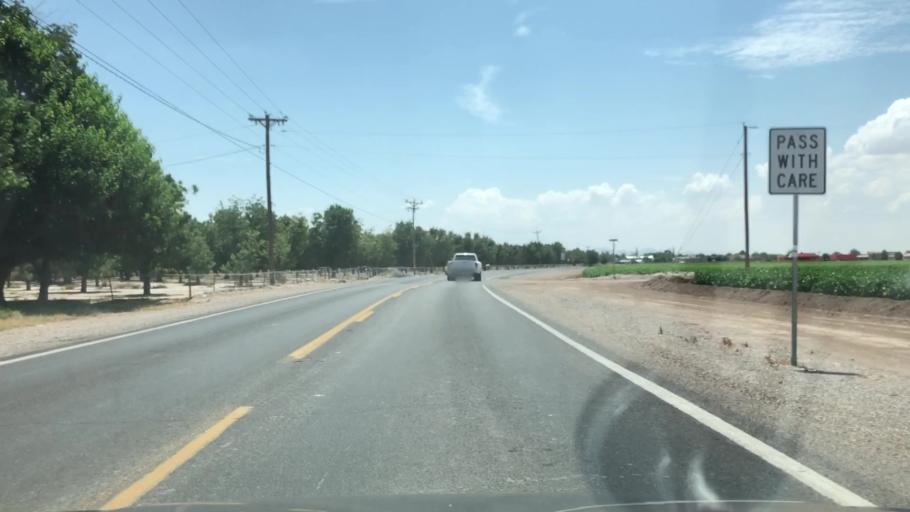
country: US
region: New Mexico
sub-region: Dona Ana County
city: La Union
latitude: 31.9639
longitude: -106.6481
